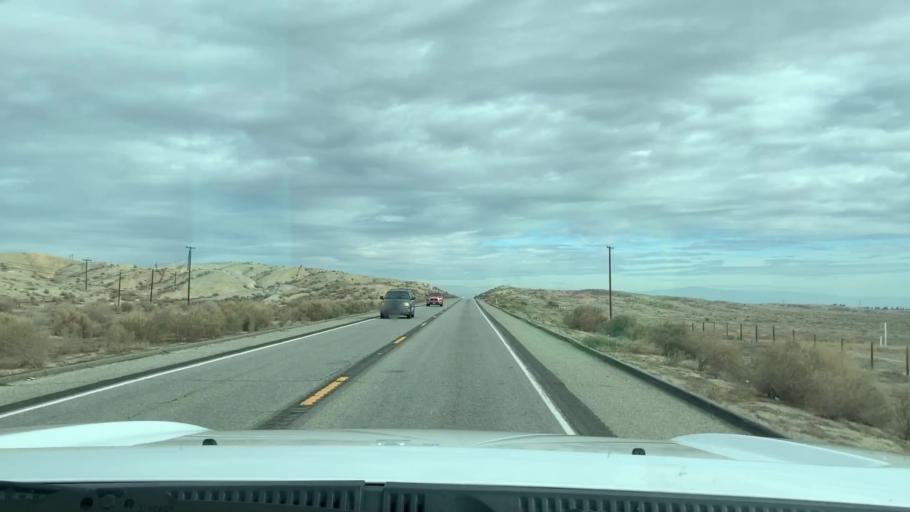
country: US
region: California
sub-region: Kern County
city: Ford City
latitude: 35.2338
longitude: -119.3686
